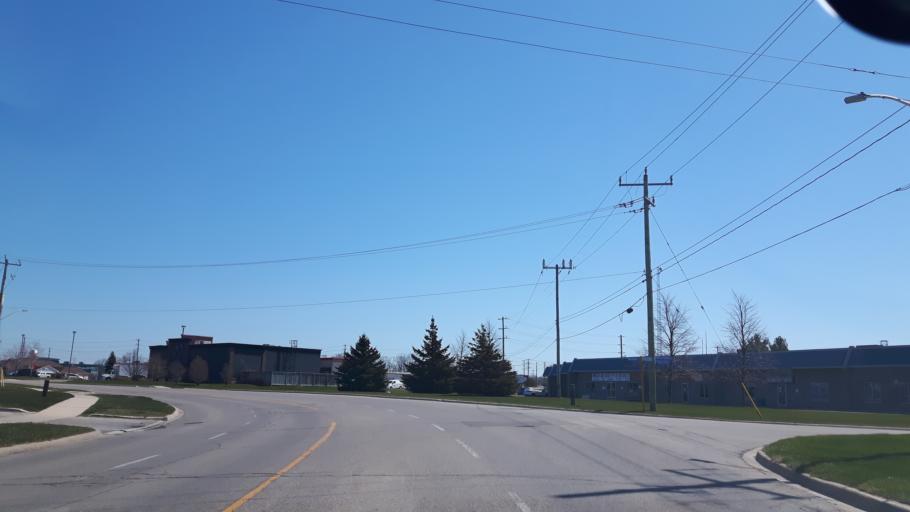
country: CA
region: Ontario
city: Goderich
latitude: 43.7316
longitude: -81.6958
